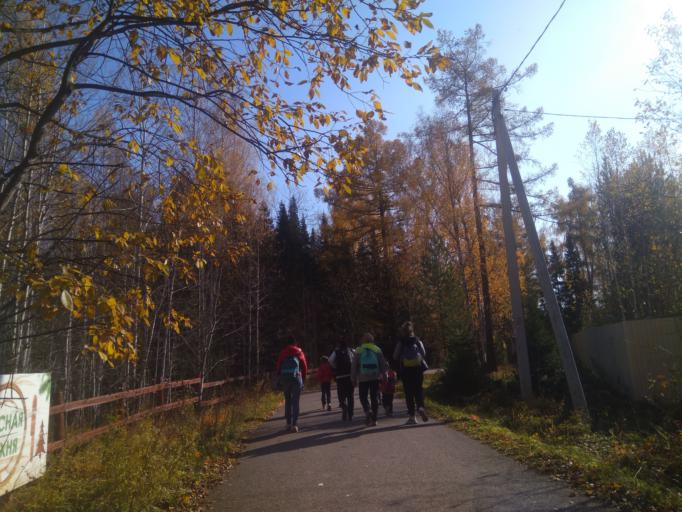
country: RU
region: Sverdlovsk
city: Mikhaylovsk
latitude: 56.5231
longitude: 59.2338
